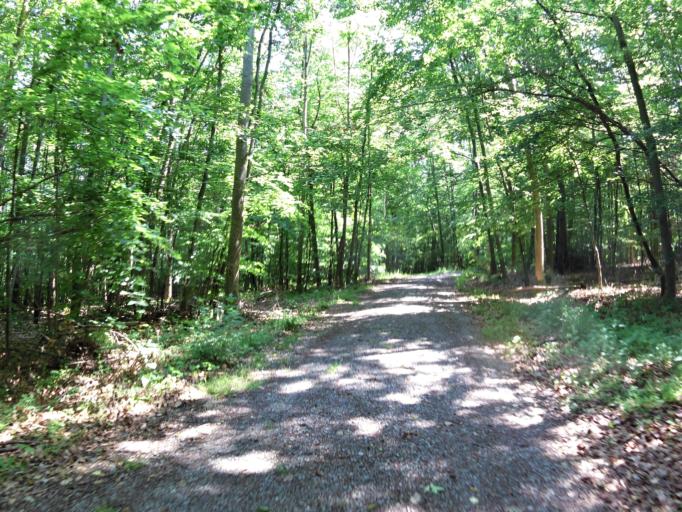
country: DE
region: Bavaria
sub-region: Regierungsbezirk Unterfranken
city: Wuerzburg
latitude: 49.7331
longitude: 9.8720
